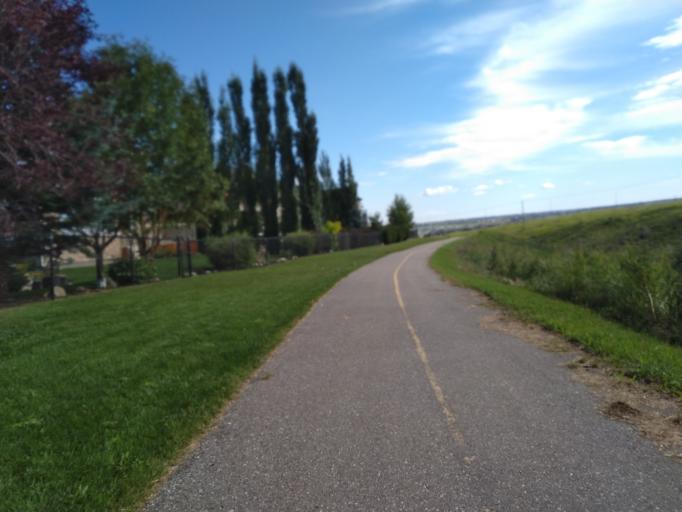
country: CA
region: Alberta
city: Calgary
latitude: 51.1563
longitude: -114.1458
